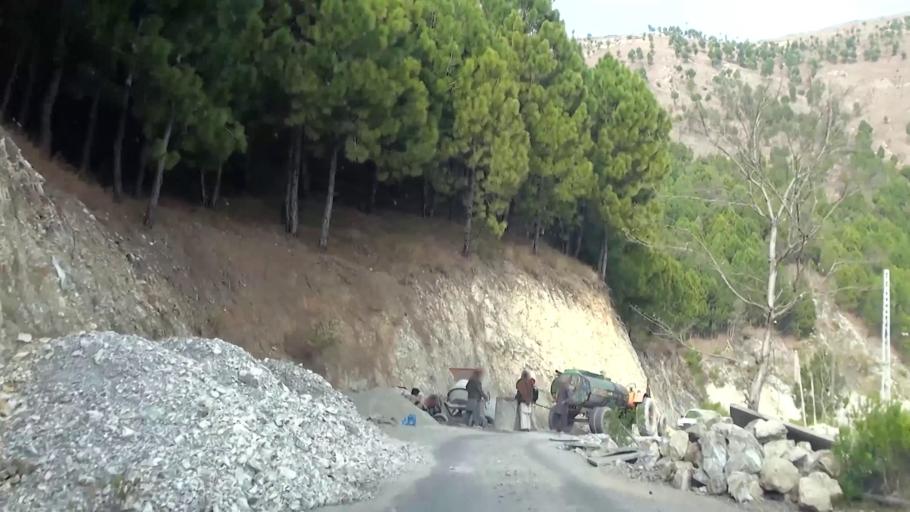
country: PK
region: Azad Kashmir
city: Muzaffarabad
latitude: 34.3662
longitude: 73.5013
